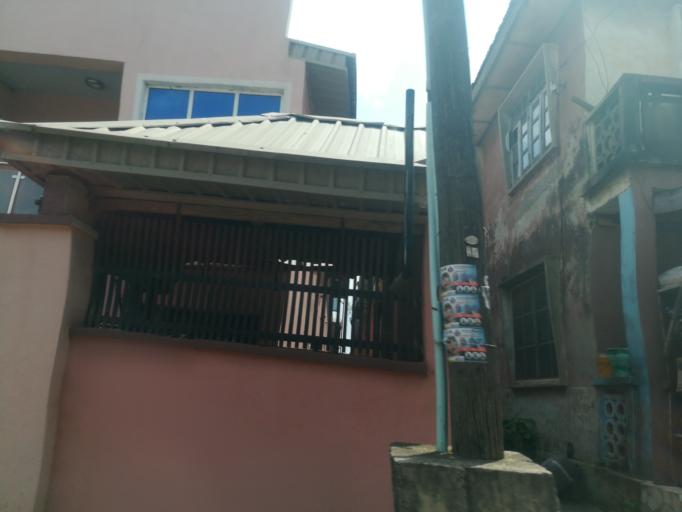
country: NG
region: Oyo
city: Ibadan
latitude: 7.3653
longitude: 3.8777
